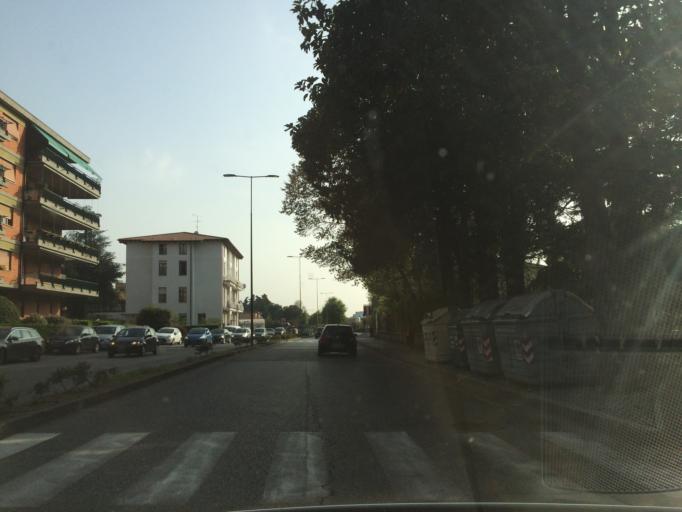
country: IT
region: Lombardy
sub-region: Provincia di Brescia
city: Brescia
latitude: 45.5196
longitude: 10.2167
